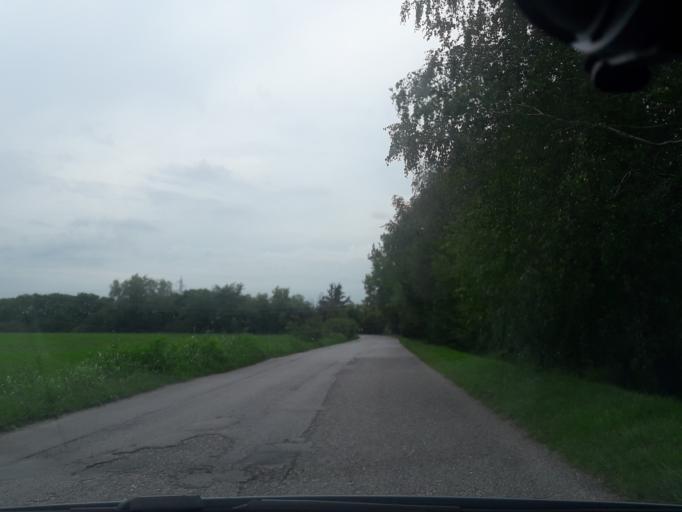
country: IT
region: Friuli Venezia Giulia
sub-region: Provincia di Udine
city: Pradamano
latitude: 46.0632
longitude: 13.2829
